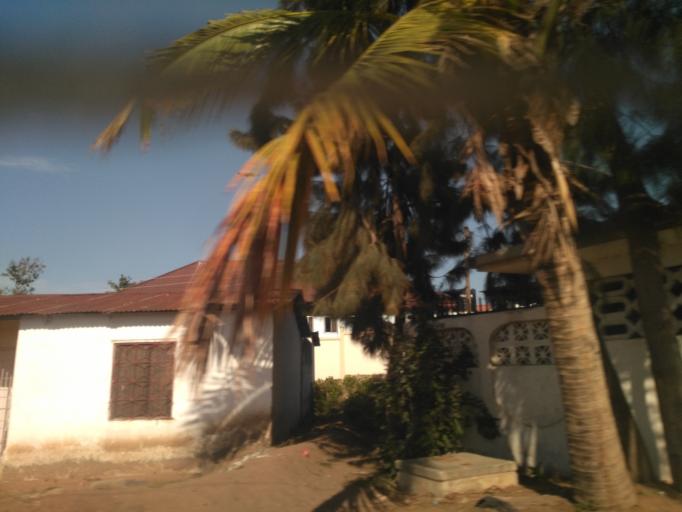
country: TZ
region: Mwanza
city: Mwanza
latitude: -2.5044
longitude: 32.8957
